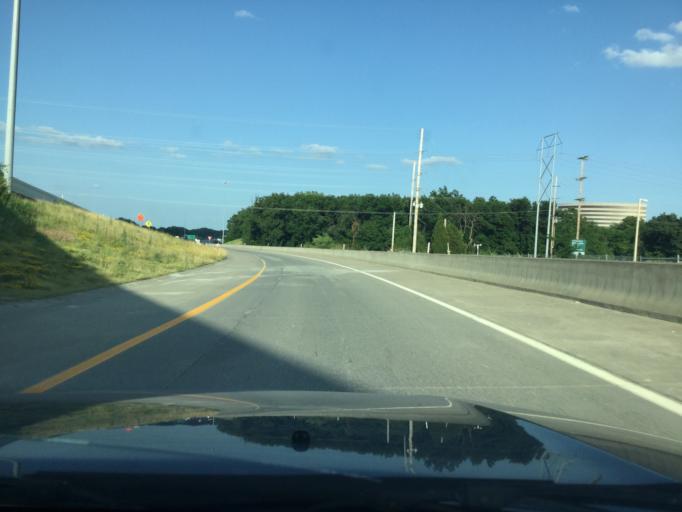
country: US
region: Kansas
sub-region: Johnson County
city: Lenexa
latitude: 38.9346
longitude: -94.7020
